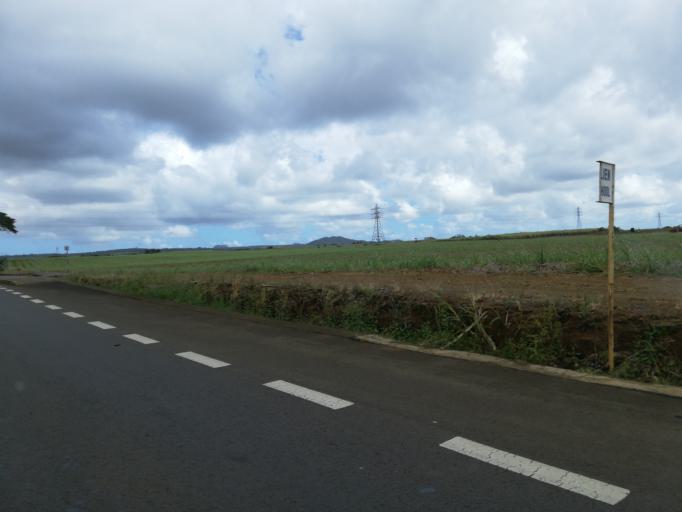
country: MU
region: Flacq
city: Queen Victoria
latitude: -20.2035
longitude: 57.6869
